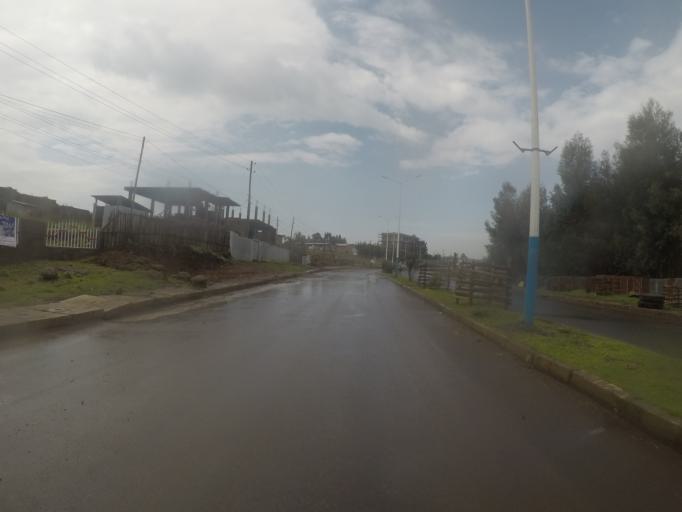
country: ET
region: Amhara
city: Debark'
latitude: 13.1432
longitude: 37.8937
